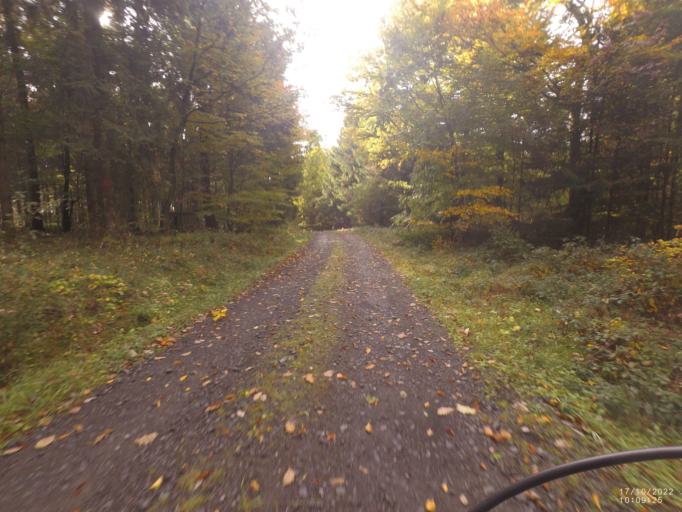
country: DE
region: Rheinland-Pfalz
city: Gefell
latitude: 50.2113
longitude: 6.9106
